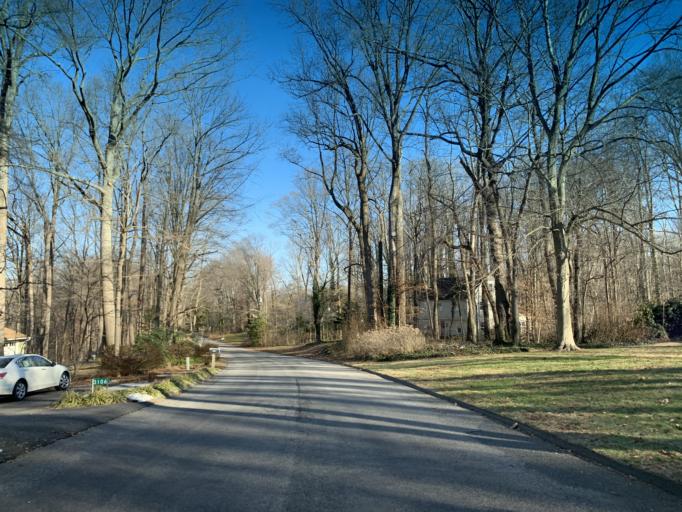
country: US
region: Maryland
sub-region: Harford County
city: South Bel Air
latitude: 39.5756
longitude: -76.2454
